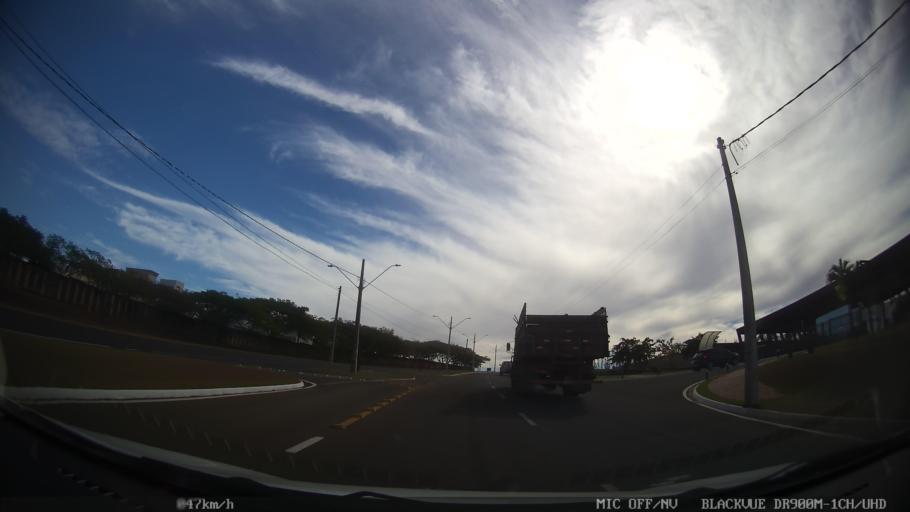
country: BR
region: Sao Paulo
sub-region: Catanduva
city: Catanduva
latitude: -21.1180
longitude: -48.9784
